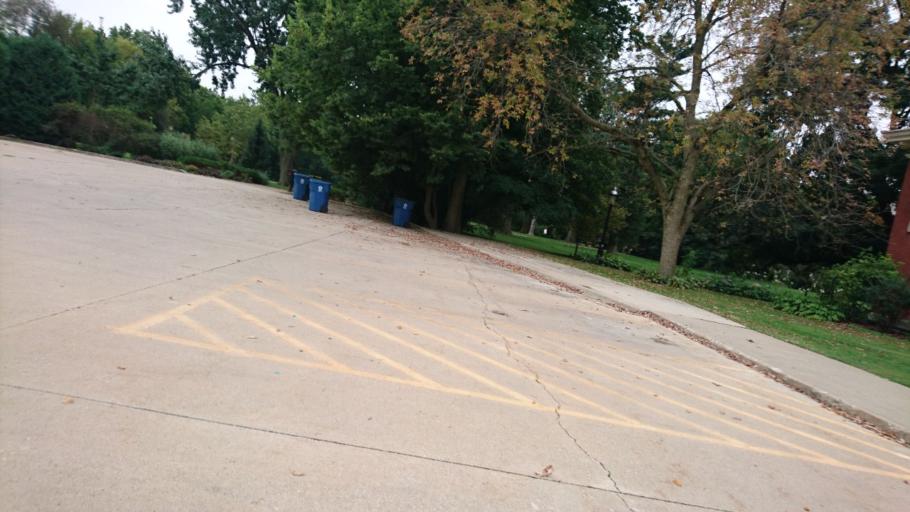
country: US
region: Illinois
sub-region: Livingston County
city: Dwight
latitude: 41.0894
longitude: -88.4280
